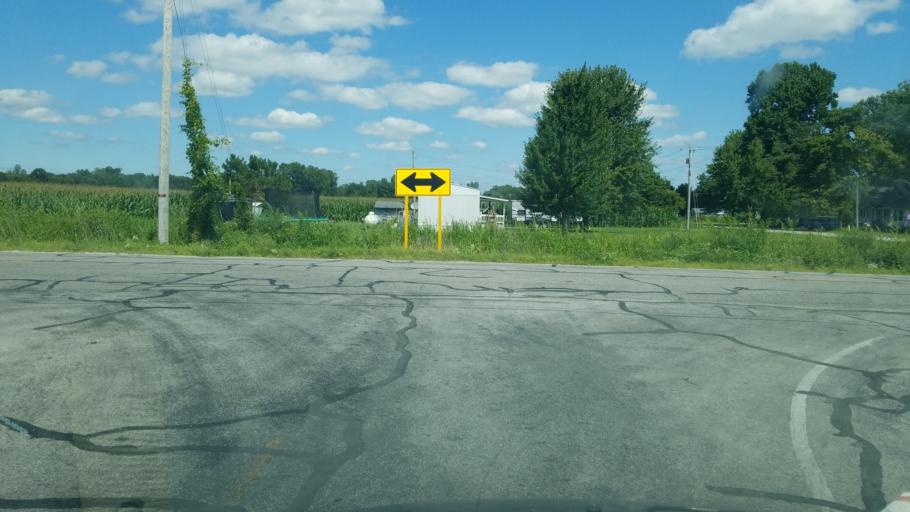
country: US
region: Ohio
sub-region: Fulton County
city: Delta
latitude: 41.5151
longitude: -83.9415
